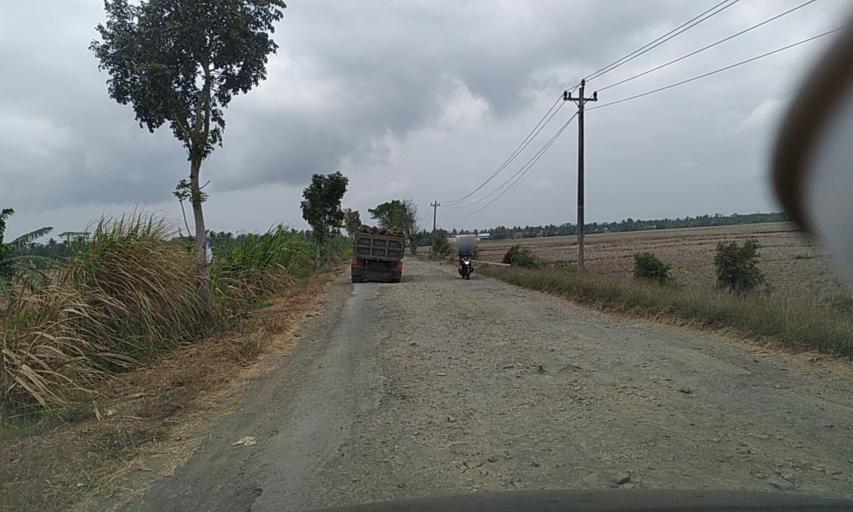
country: ID
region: Central Java
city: Jeruklegi
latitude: -7.6385
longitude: 108.9508
